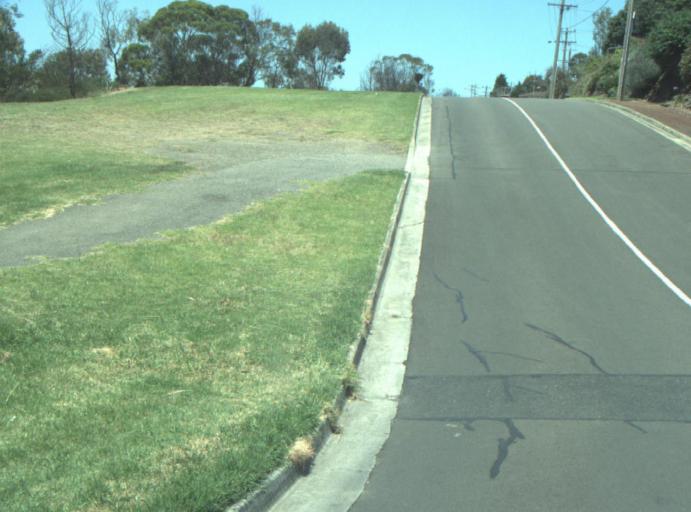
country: AU
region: Victoria
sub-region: Greater Geelong
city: Wandana Heights
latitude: -38.1570
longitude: 144.3199
